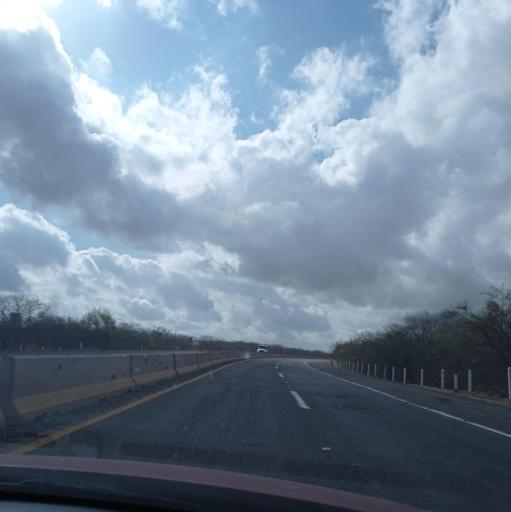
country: MX
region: Sinaloa
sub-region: Navolato
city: Juan Aldama (El Tigre)
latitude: 24.9939
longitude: -107.7753
